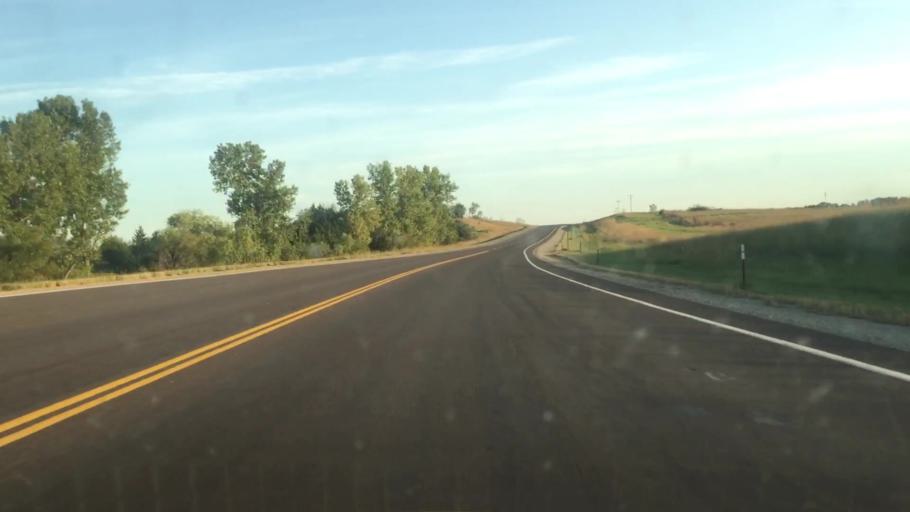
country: US
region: Kansas
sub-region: Atchison County
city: Atchison
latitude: 39.4668
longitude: -95.0948
